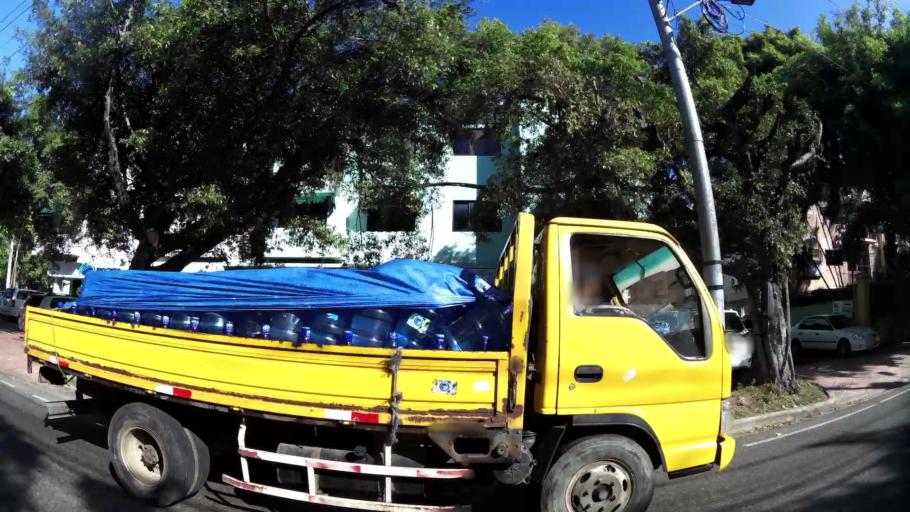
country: DO
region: Nacional
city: Ciudad Nueva
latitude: 18.4634
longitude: -69.9022
